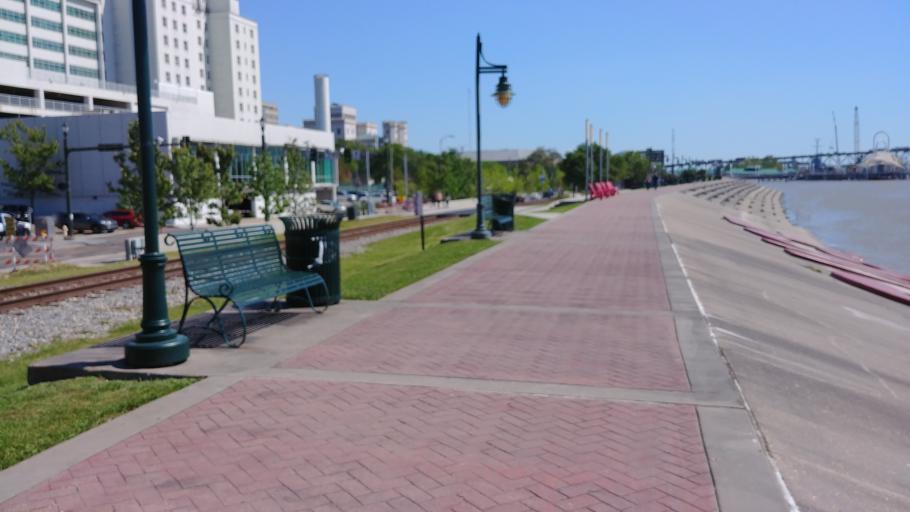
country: US
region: Louisiana
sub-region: West Baton Rouge Parish
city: Port Allen
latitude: 30.4498
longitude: -91.1908
